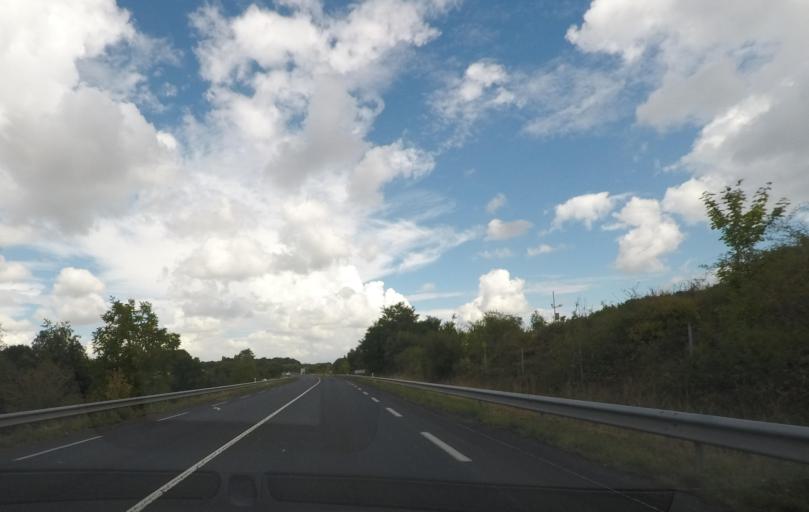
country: FR
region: Pays de la Loire
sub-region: Departement de la Sarthe
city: Champagne
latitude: 48.0390
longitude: 0.2939
